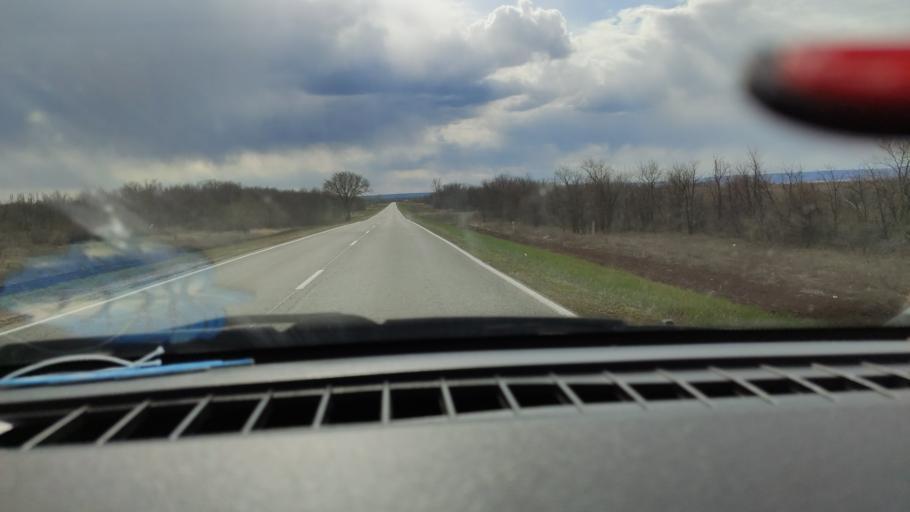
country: RU
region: Saratov
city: Privolzhskiy
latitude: 51.2842
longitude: 45.9657
